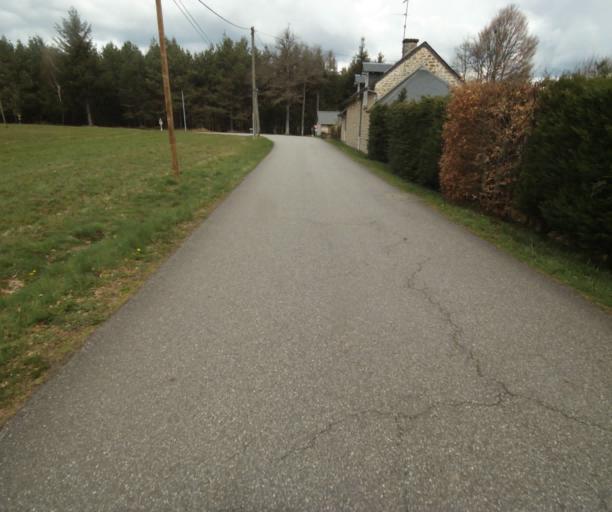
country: FR
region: Limousin
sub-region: Departement de la Correze
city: Correze
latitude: 45.3338
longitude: 1.9209
